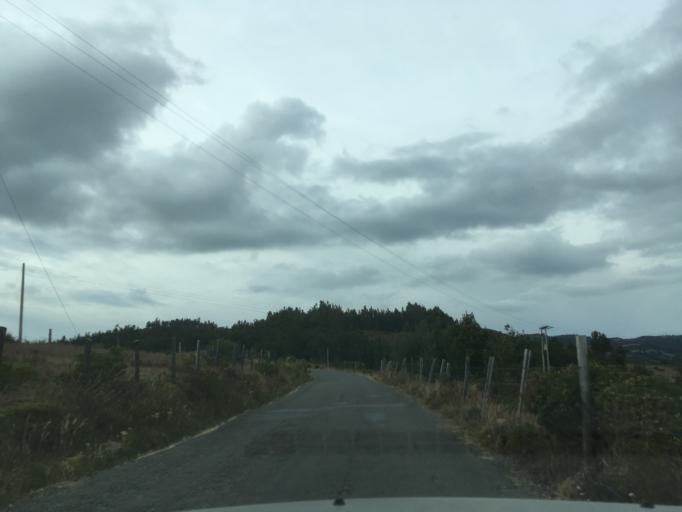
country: CO
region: Boyaca
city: Firavitoba
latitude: 5.6785
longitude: -73.0217
